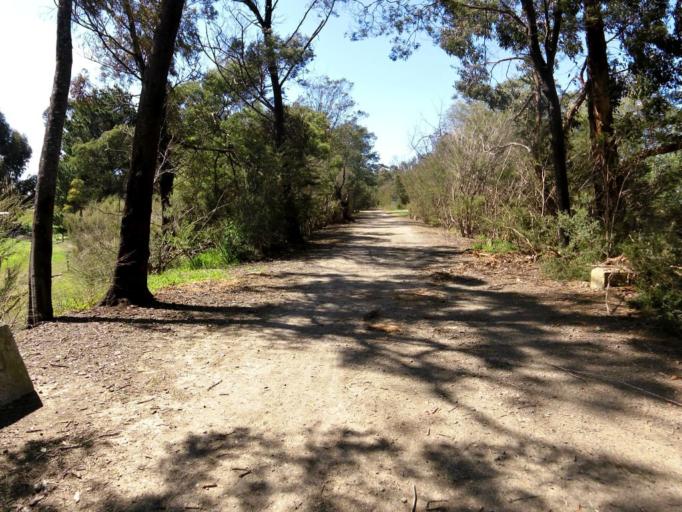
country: AU
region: Victoria
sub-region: Latrobe
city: Moe
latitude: -38.1752
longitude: 146.2750
